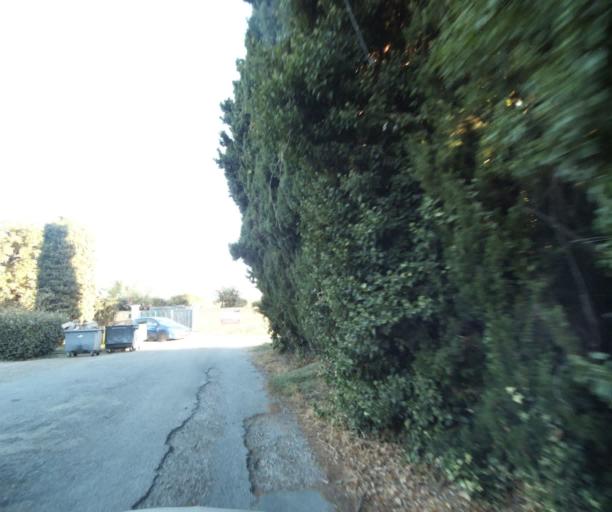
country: FR
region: Languedoc-Roussillon
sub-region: Departement du Gard
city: Bouillargues
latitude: 43.8075
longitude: 4.4052
